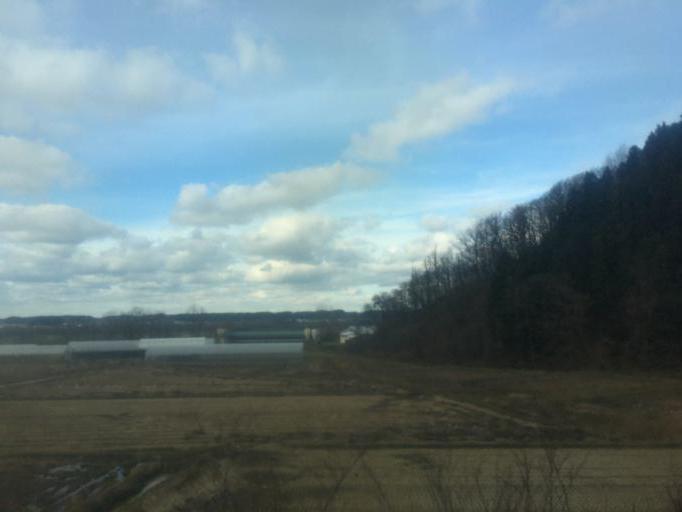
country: JP
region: Akita
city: Noshiromachi
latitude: 40.2108
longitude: 140.1357
